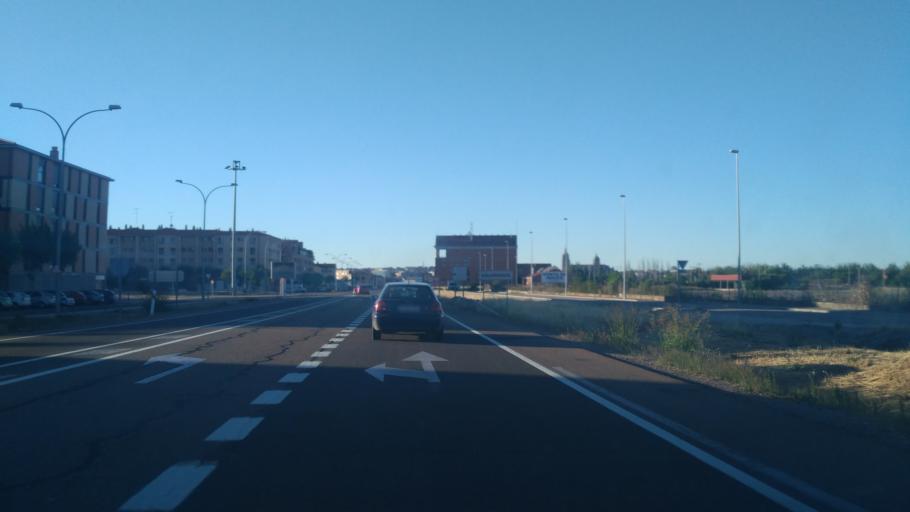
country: ES
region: Castille and Leon
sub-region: Provincia de Salamanca
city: Carbajosa de la Sagrada
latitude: 40.9436
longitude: -5.6692
